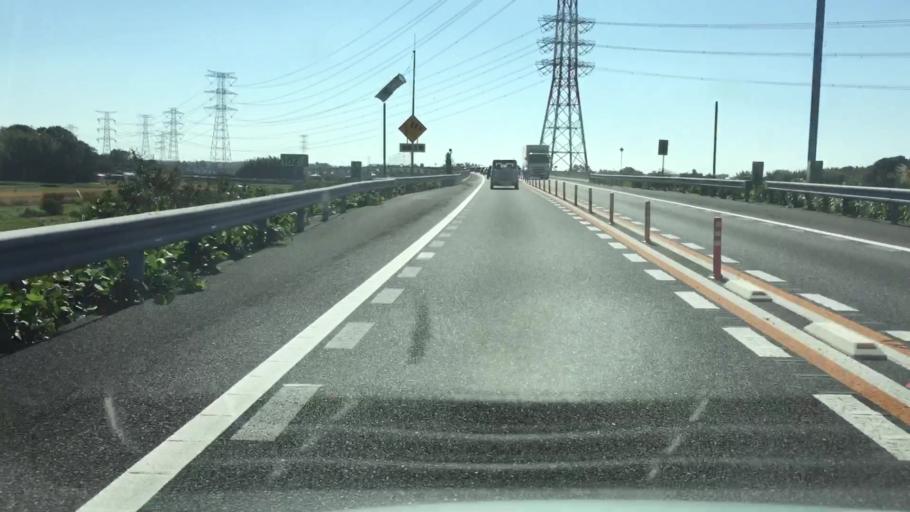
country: JP
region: Ibaraki
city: Ushiku
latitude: 36.0027
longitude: 140.1469
